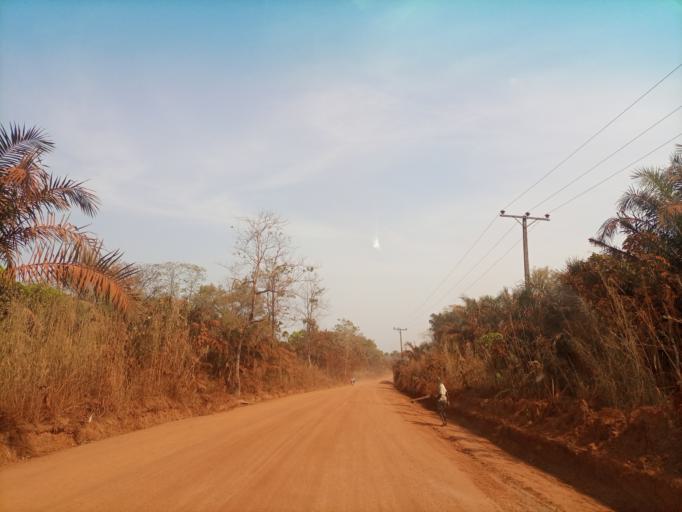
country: NG
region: Enugu
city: Eha Amufu
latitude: 6.6739
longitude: 7.7320
